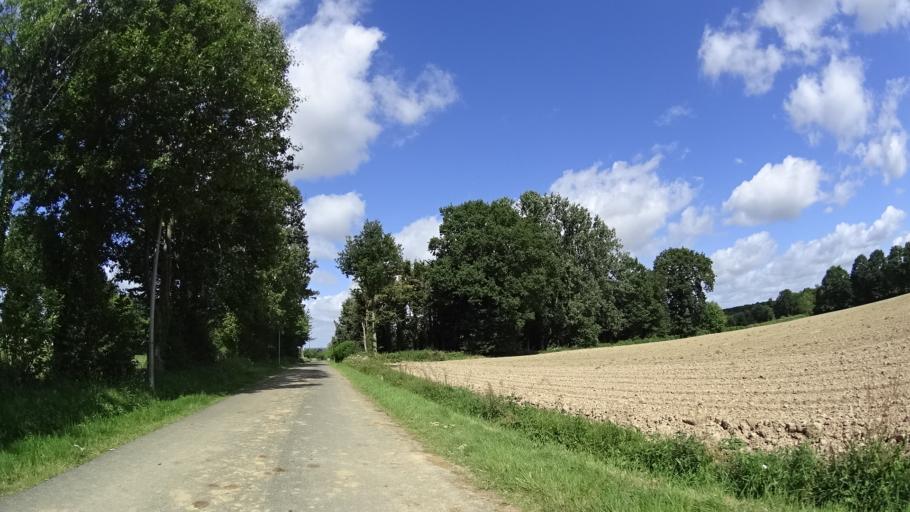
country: FR
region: Brittany
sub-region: Departement d'Ille-et-Vilaine
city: La Meziere
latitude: 48.2338
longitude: -1.7440
